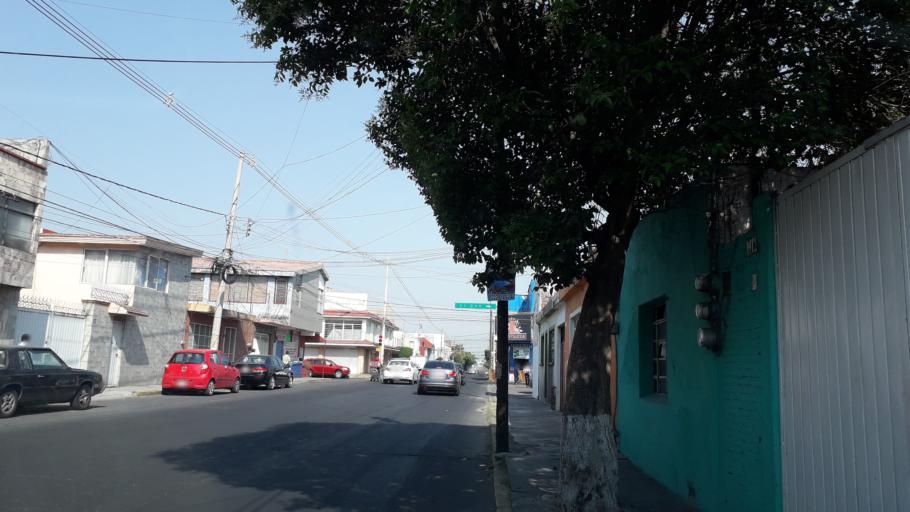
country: MX
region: Puebla
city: Puebla
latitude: 19.0434
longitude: -98.2179
